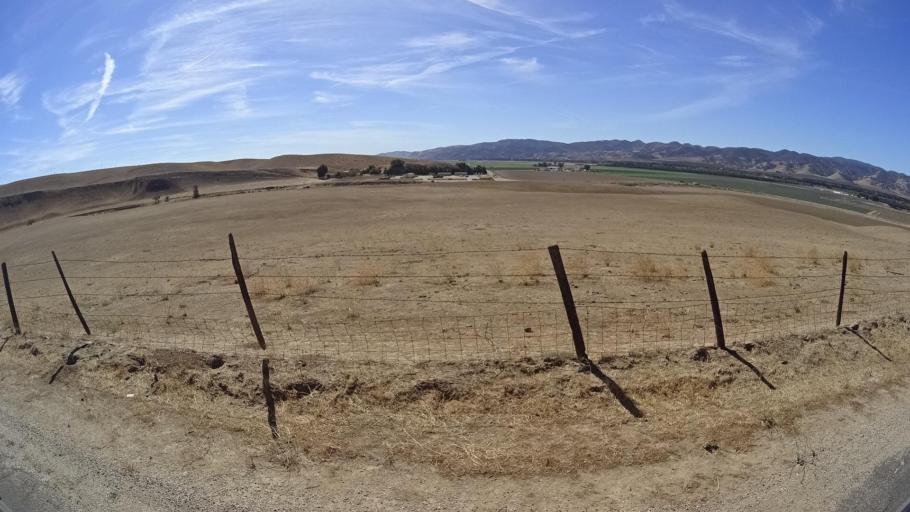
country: US
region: California
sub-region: San Luis Obispo County
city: Lake Nacimiento
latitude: 36.0247
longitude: -120.8852
